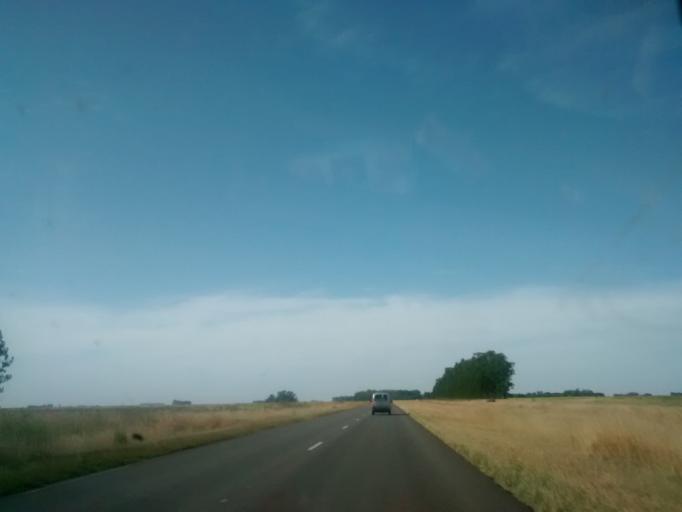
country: AR
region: Buenos Aires
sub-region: Partido de Ayacucho
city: Ayacucho
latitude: -37.3974
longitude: -58.4876
